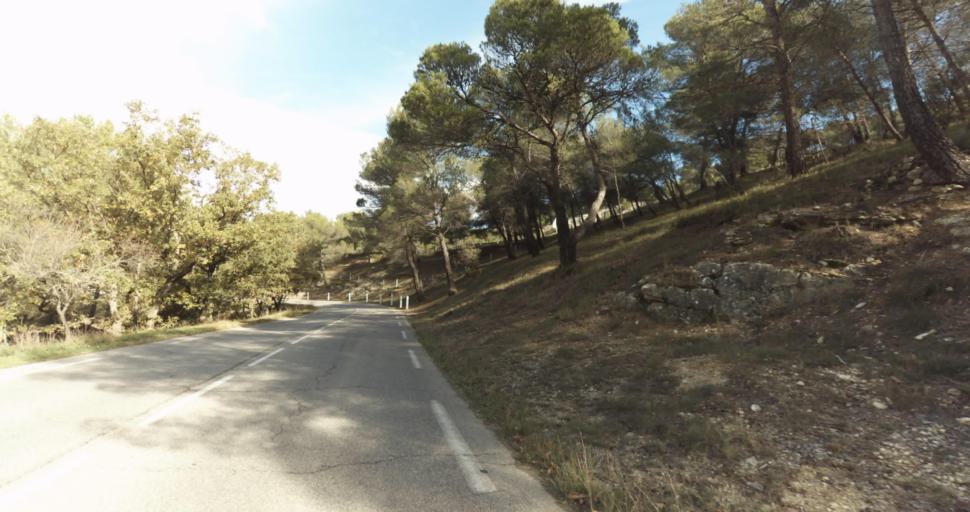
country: FR
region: Provence-Alpes-Cote d'Azur
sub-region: Departement des Bouches-du-Rhone
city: Venelles
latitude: 43.6032
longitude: 5.4958
